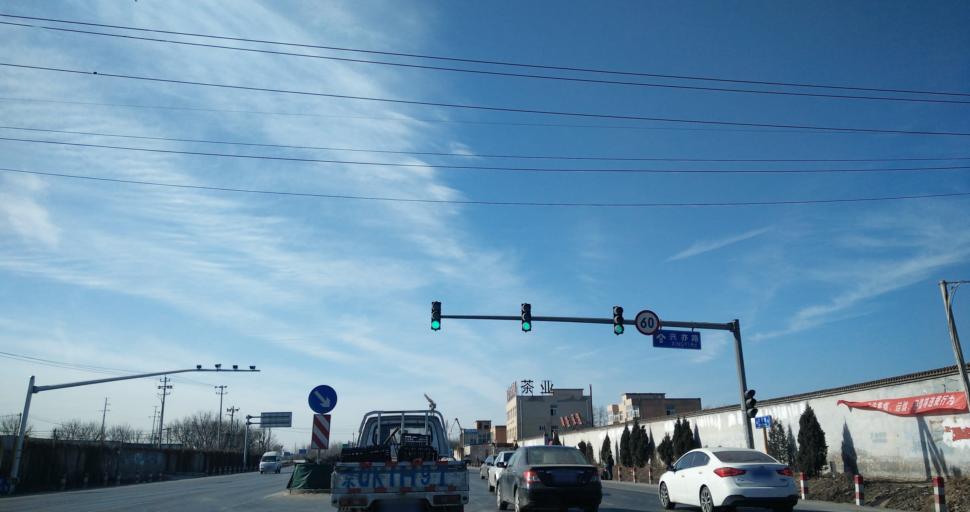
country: CN
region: Beijing
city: Yinghai
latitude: 39.7441
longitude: 116.4563
